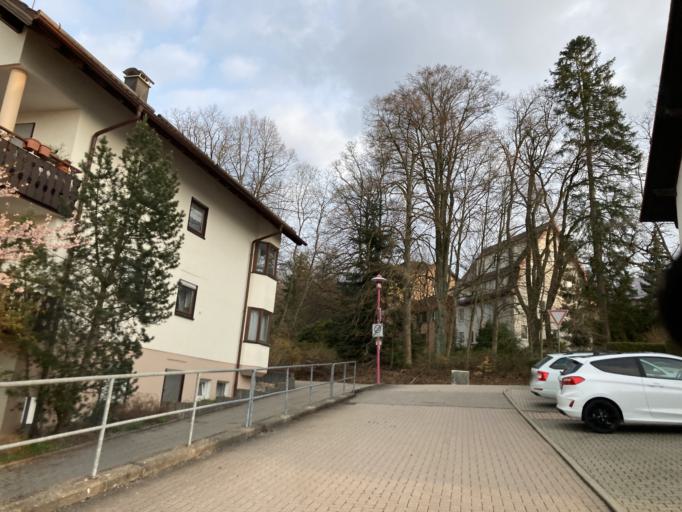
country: DE
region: Baden-Wuerttemberg
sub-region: Karlsruhe Region
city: Schomberg
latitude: 48.7881
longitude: 8.6527
